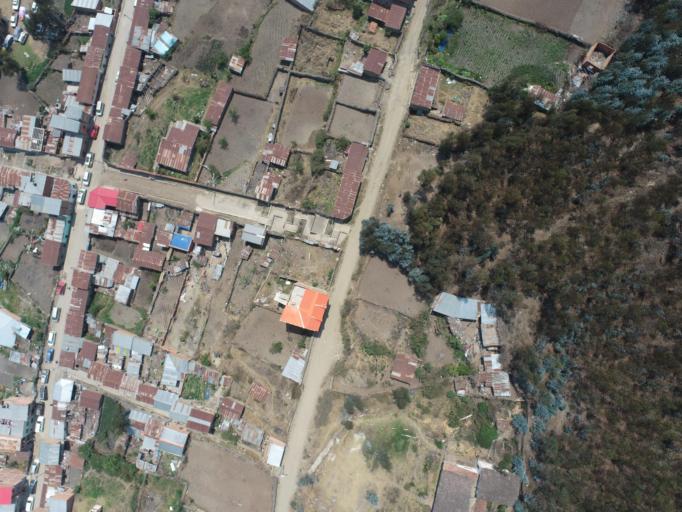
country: BO
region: La Paz
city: Quime
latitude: -16.9831
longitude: -67.2172
